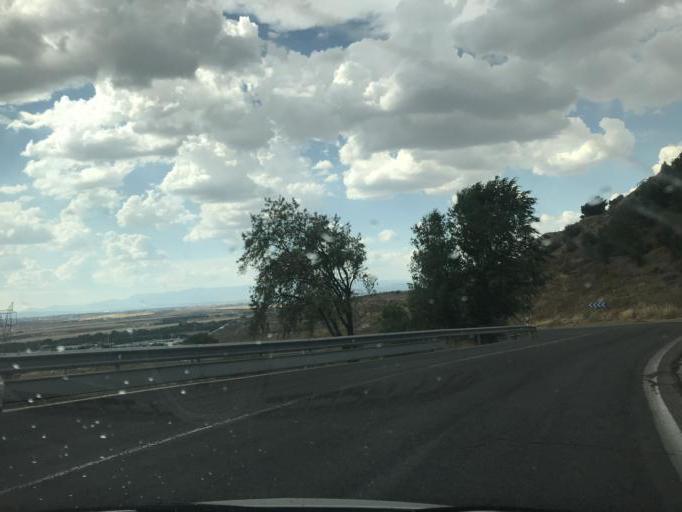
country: ES
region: Madrid
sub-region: Provincia de Madrid
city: Paracuellos de Jarama
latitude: 40.5053
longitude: -3.5345
